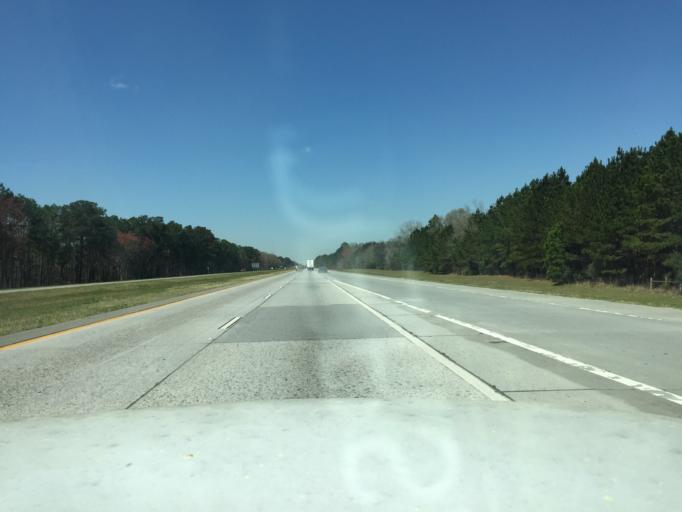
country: US
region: Georgia
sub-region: Chatham County
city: Bloomingdale
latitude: 32.0868
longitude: -81.2870
